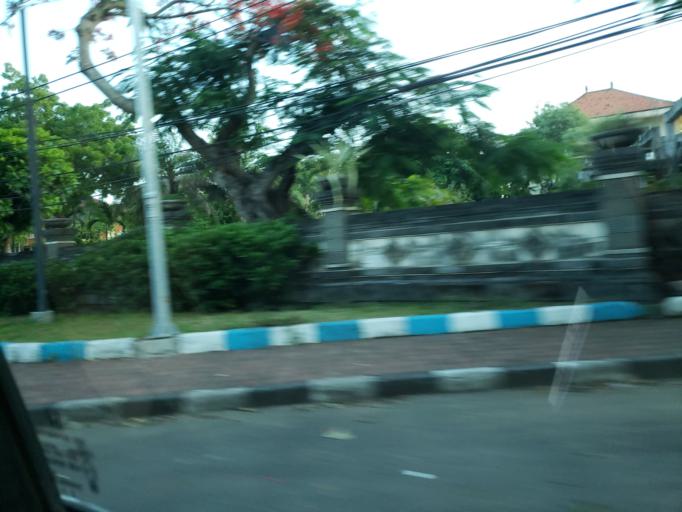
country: ID
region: Bali
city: Jimbaran
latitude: -8.7985
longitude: 115.1619
